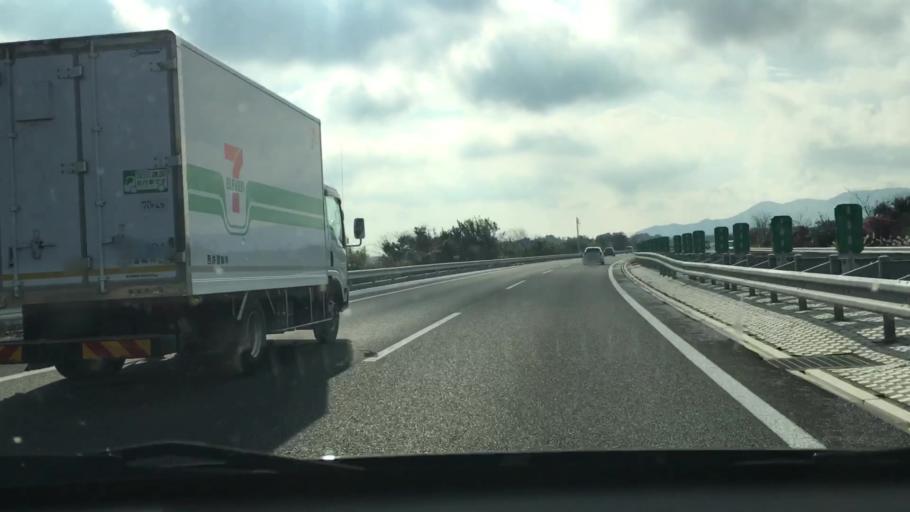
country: JP
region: Kumamoto
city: Uto
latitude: 32.7159
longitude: 130.7674
